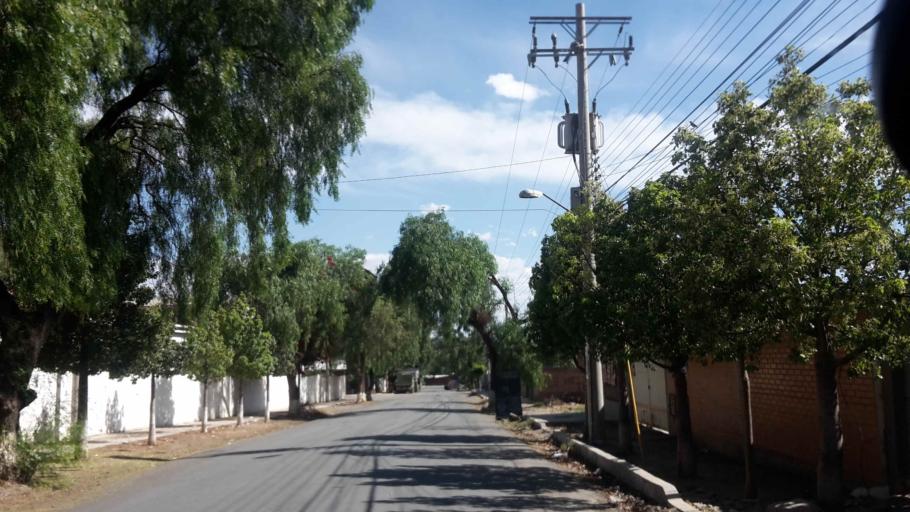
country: BO
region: Cochabamba
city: Cochabamba
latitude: -17.3349
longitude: -66.2263
